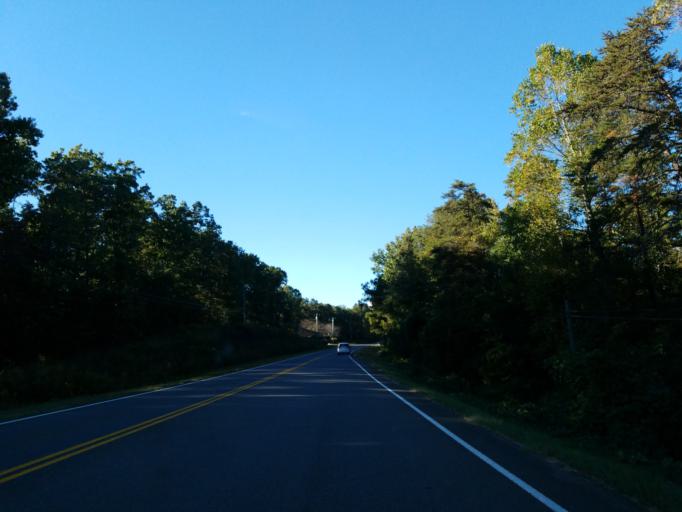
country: US
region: Georgia
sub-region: Pickens County
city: Nelson
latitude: 34.3938
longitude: -84.3805
